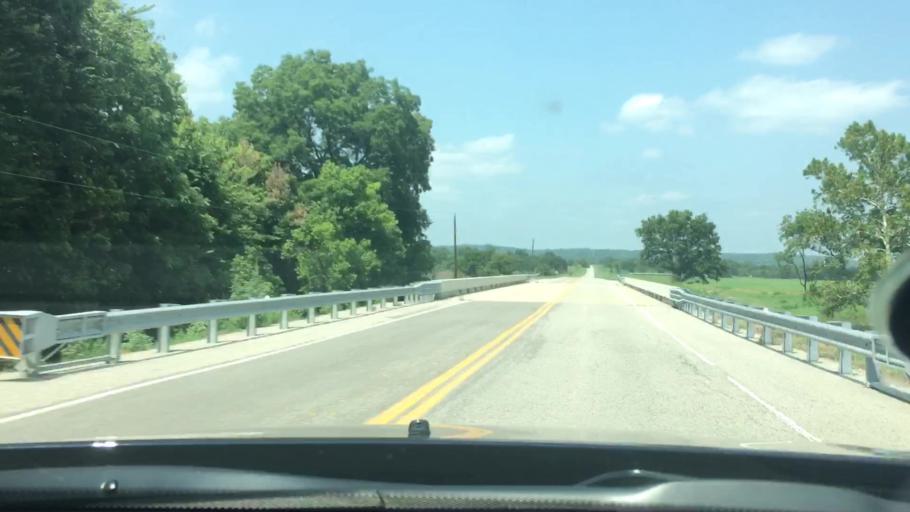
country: US
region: Oklahoma
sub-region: Johnston County
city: Tishomingo
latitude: 34.3889
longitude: -96.4962
